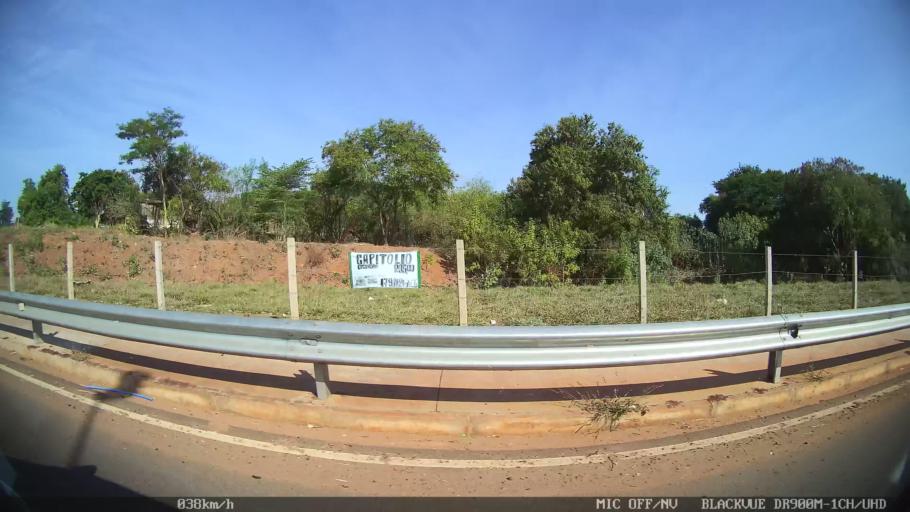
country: BR
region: Sao Paulo
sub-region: Sao Jose Do Rio Preto
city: Sao Jose do Rio Preto
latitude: -20.7901
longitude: -49.3902
